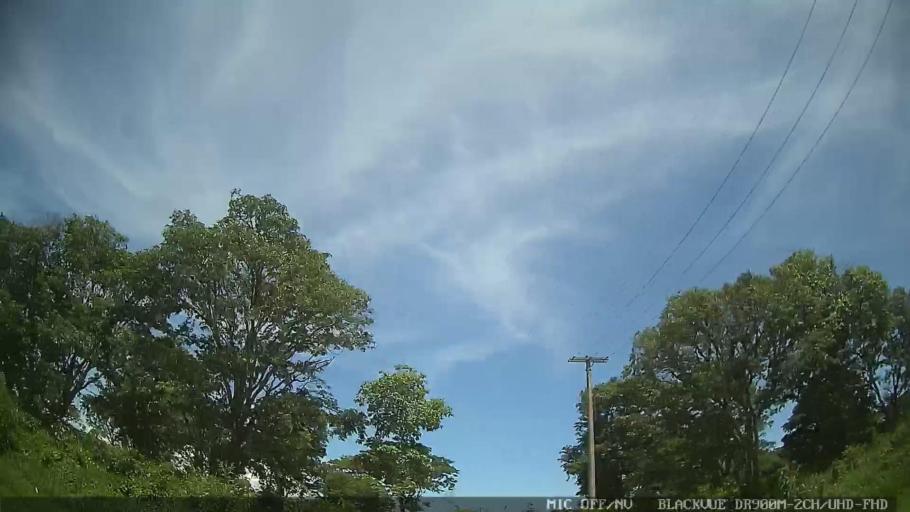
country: BR
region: Sao Paulo
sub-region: Jaguariuna
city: Jaguariuna
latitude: -22.6756
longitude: -47.0038
